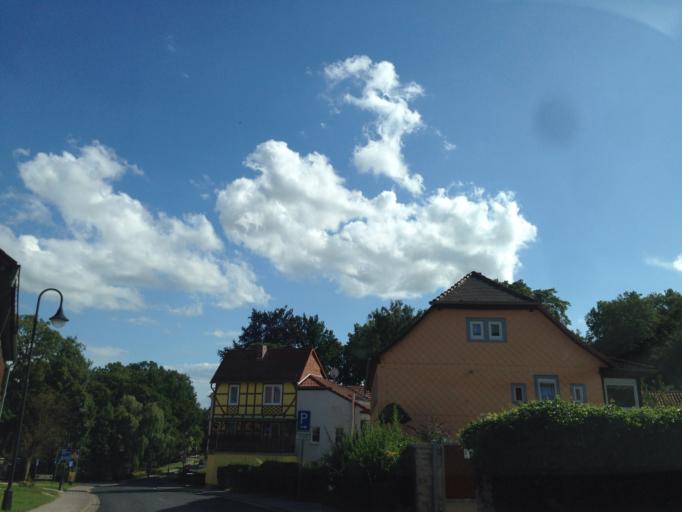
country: DE
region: Thuringia
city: Blankenhain
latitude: 50.8636
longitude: 11.3402
